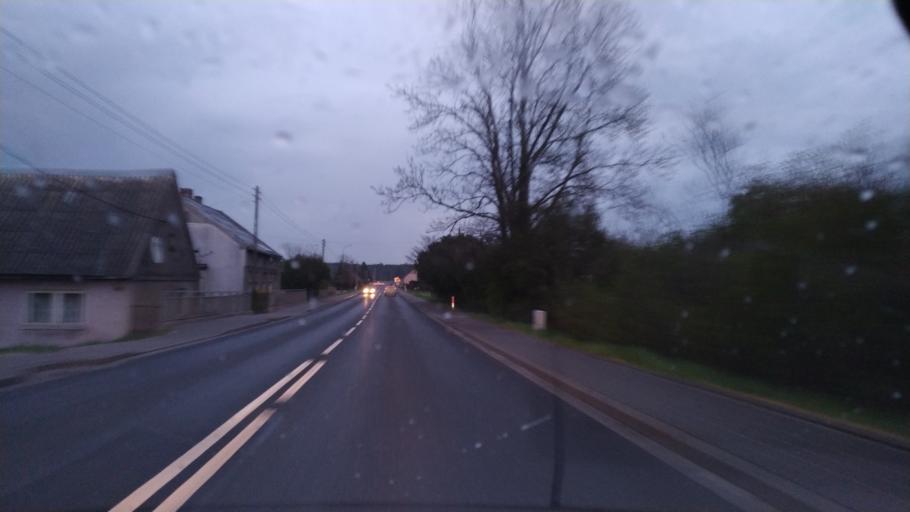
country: PL
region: Greater Poland Voivodeship
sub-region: Powiat pilski
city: Szydlowo
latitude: 53.2468
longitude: 16.5932
